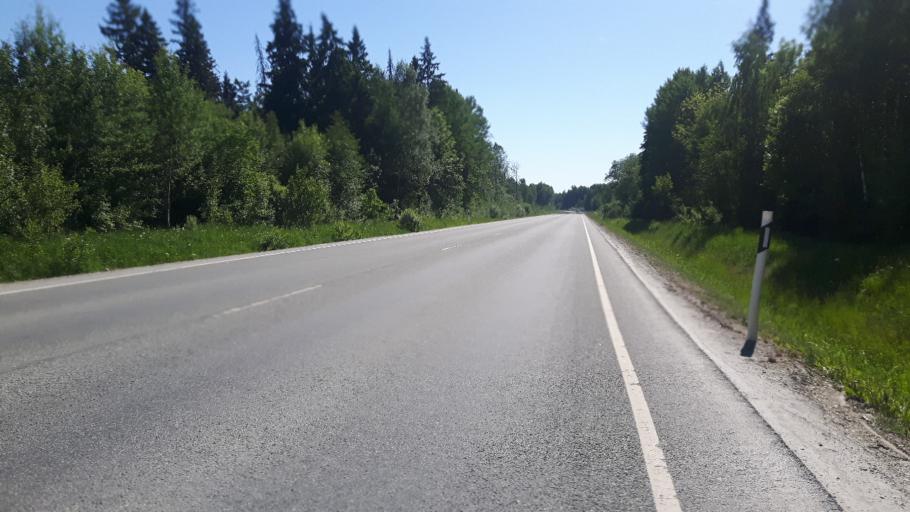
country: EE
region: Raplamaa
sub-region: Rapla vald
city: Rapla
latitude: 59.0292
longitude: 24.8202
